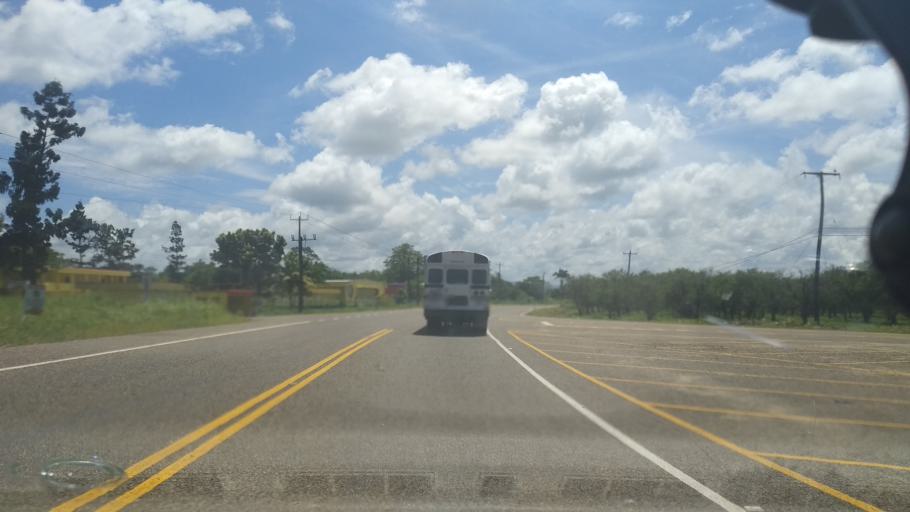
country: BZ
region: Stann Creek
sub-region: Dangriga
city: Dangriga
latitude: 16.9982
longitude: -88.3148
